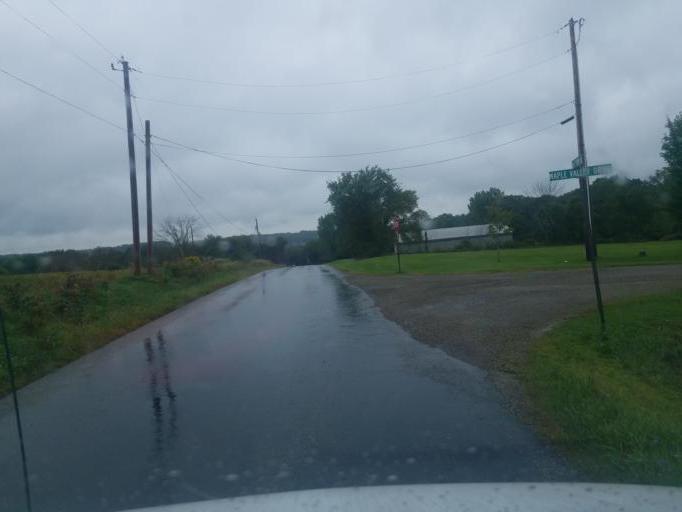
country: US
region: Ohio
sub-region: Medina County
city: Lodi
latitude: 40.9745
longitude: -82.0193
